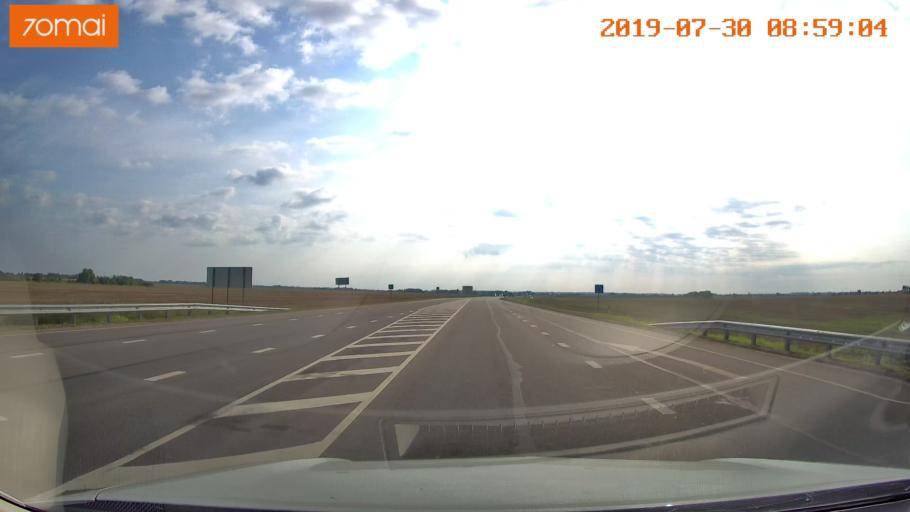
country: RU
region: Kaliningrad
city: Gusev
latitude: 54.6132
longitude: 22.1451
